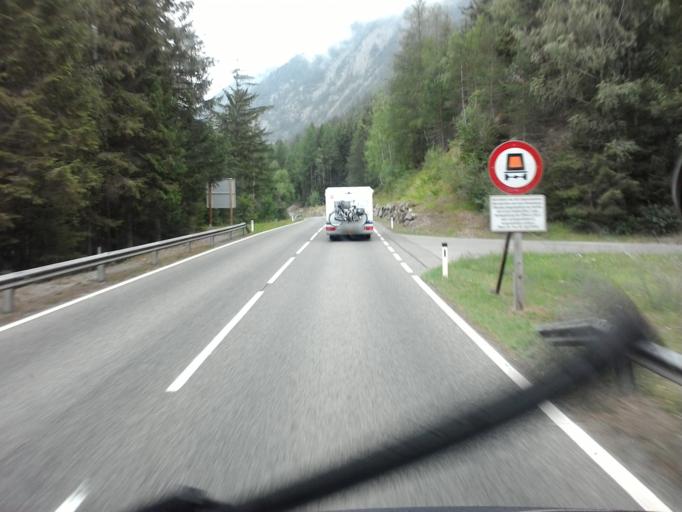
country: AT
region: Tyrol
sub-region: Politischer Bezirk Lienz
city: Matrei in Osttirol
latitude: 47.0116
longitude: 12.5395
